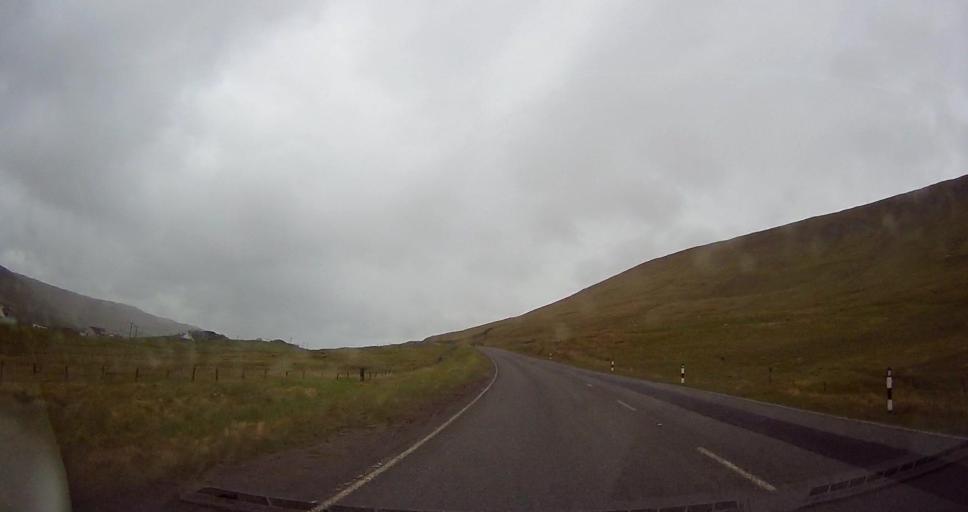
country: GB
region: Scotland
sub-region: Shetland Islands
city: Lerwick
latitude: 60.2536
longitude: -1.2977
